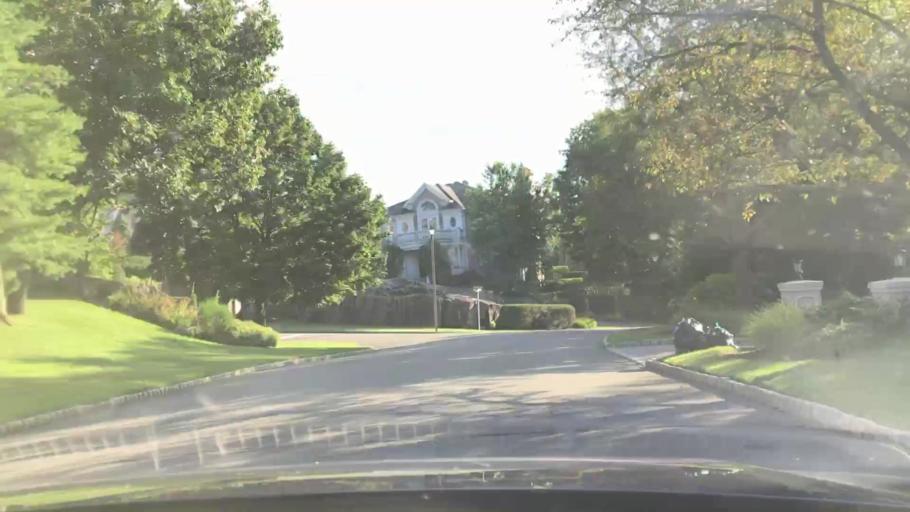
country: US
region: New Jersey
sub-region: Bergen County
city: Tenafly
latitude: 40.9295
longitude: -73.9452
